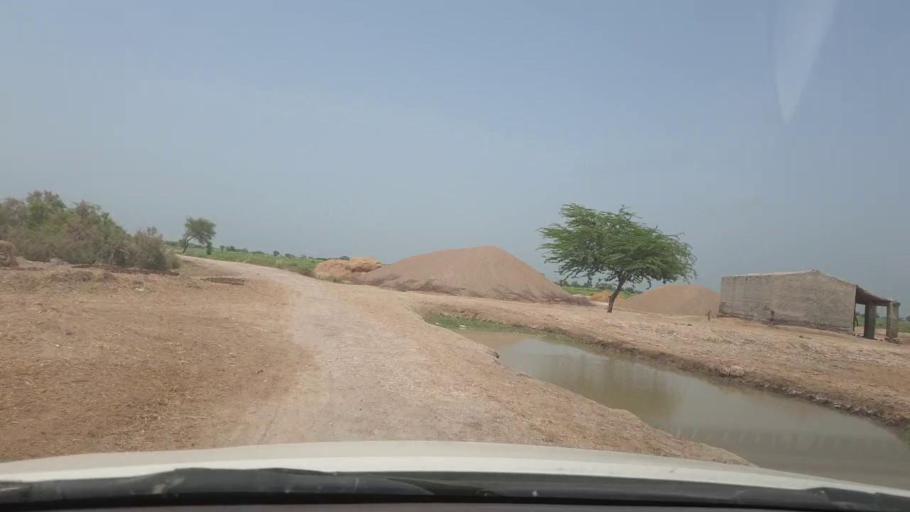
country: PK
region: Sindh
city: Shikarpur
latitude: 28.0726
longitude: 68.5749
